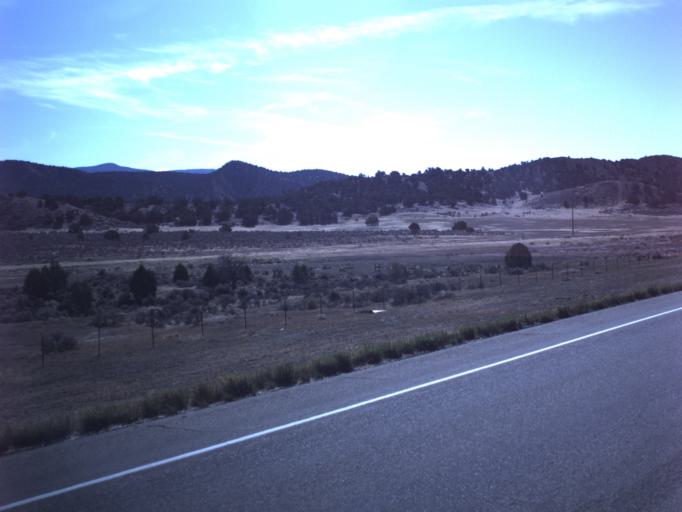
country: US
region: Utah
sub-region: Sanpete County
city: Gunnison
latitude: 39.3843
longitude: -111.9278
